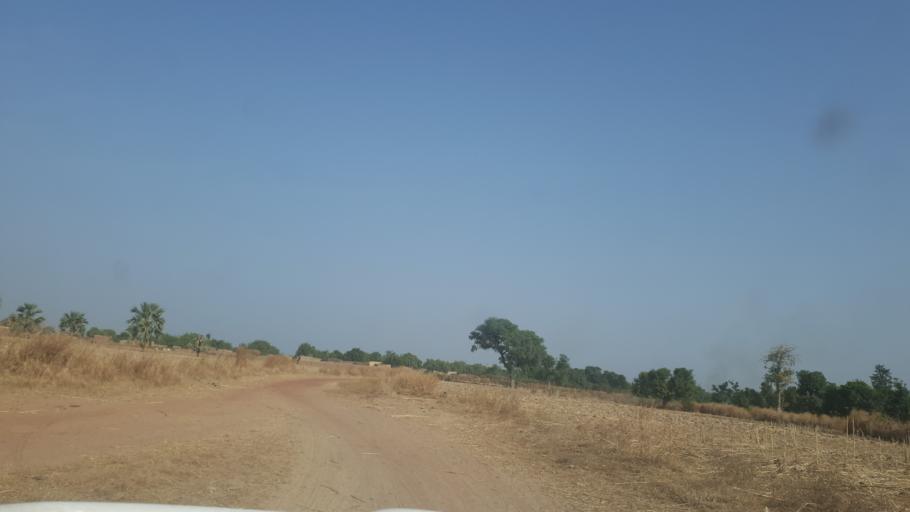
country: ML
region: Segou
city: Baroueli
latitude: 13.3534
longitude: -6.9364
